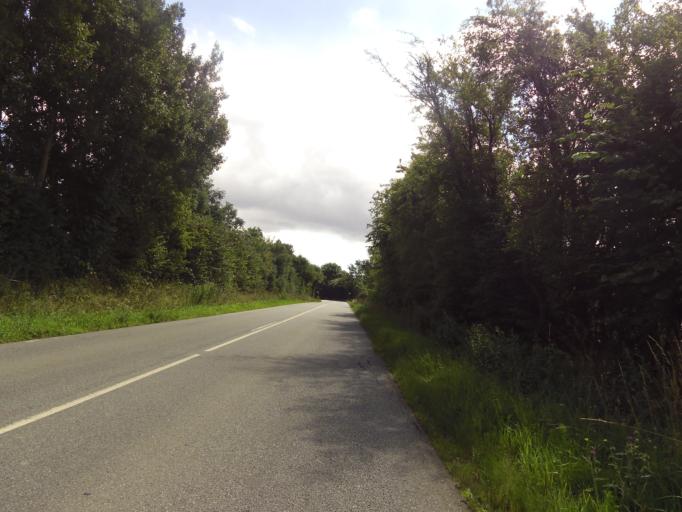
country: DK
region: South Denmark
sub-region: Haderslev Kommune
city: Haderslev
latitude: 55.2586
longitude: 9.4440
